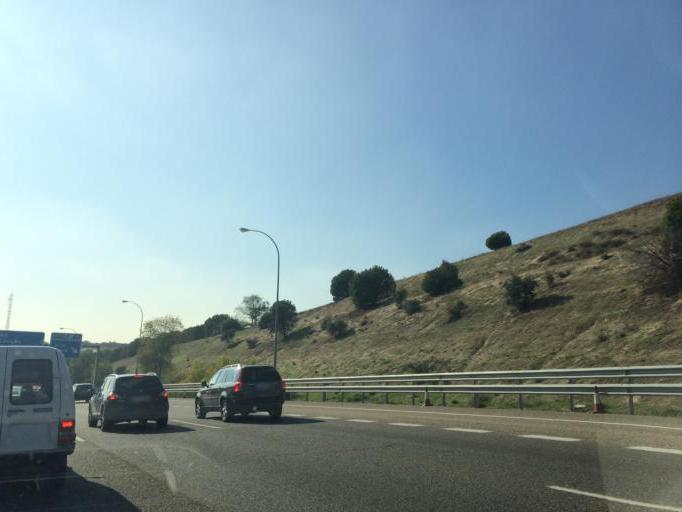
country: ES
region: Madrid
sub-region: Provincia de Madrid
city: Fuencarral-El Pardo
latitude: 40.4901
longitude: -3.7393
